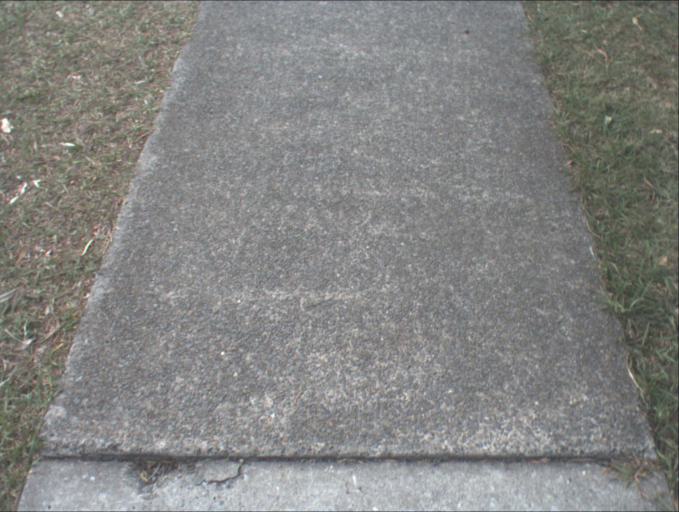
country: AU
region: Queensland
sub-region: Logan
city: Logan City
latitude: -27.6381
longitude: 153.1066
